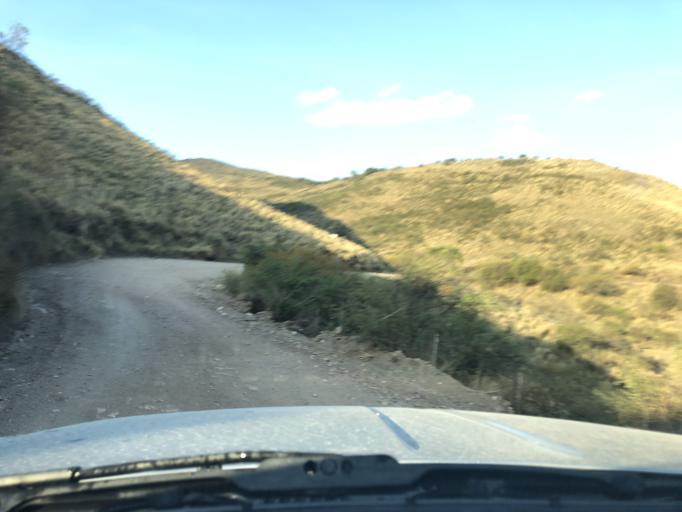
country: AR
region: Cordoba
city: Agua de Oro
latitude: -31.0554
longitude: -64.3547
